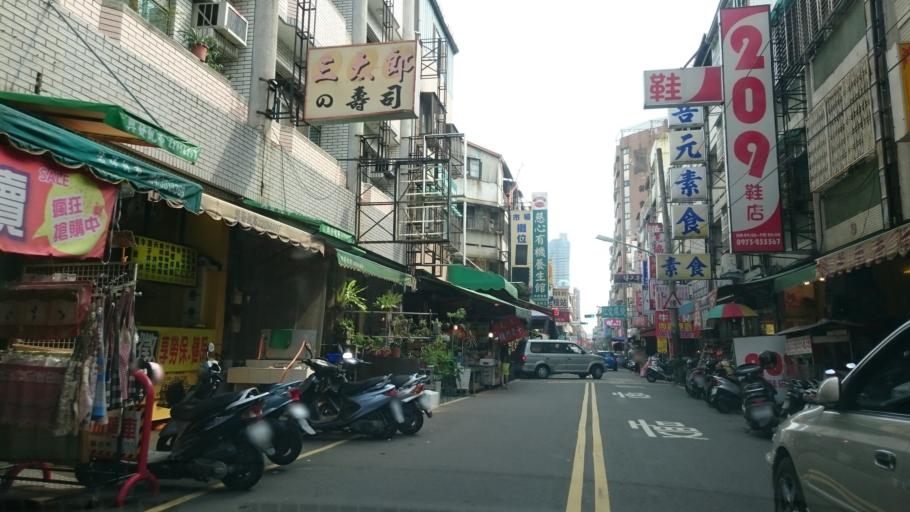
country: TW
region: Taiwan
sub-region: Taichung City
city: Taichung
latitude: 24.1477
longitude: 120.6587
